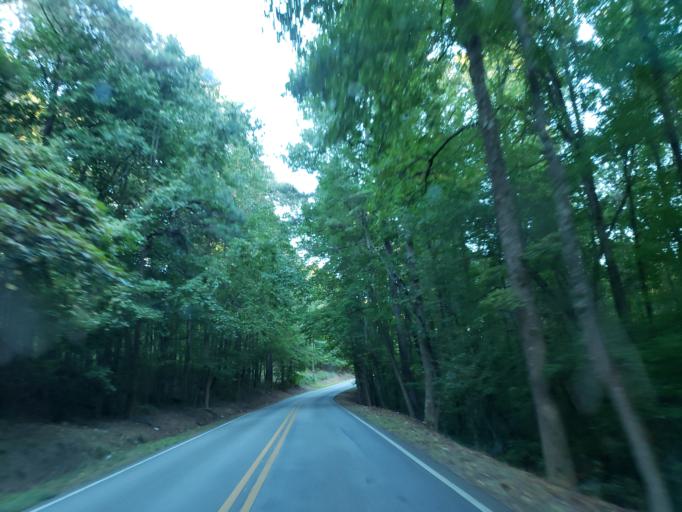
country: US
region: Georgia
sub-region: Bartow County
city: Rydal
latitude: 34.3596
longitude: -84.5777
